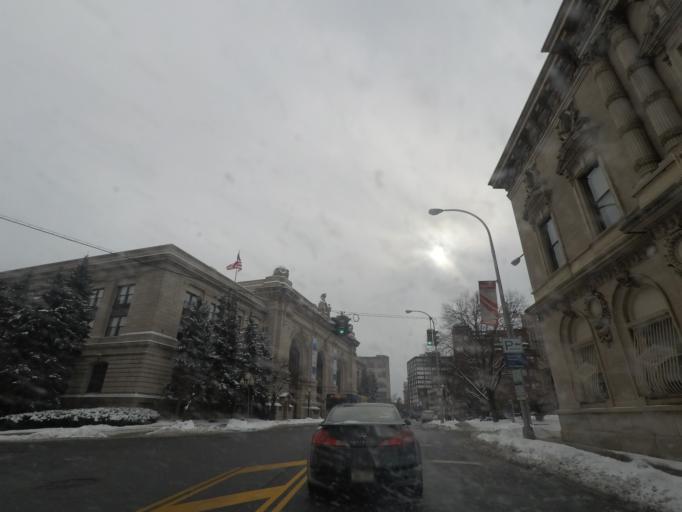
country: US
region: New York
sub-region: Albany County
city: Albany
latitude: 42.6522
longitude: -73.7495
